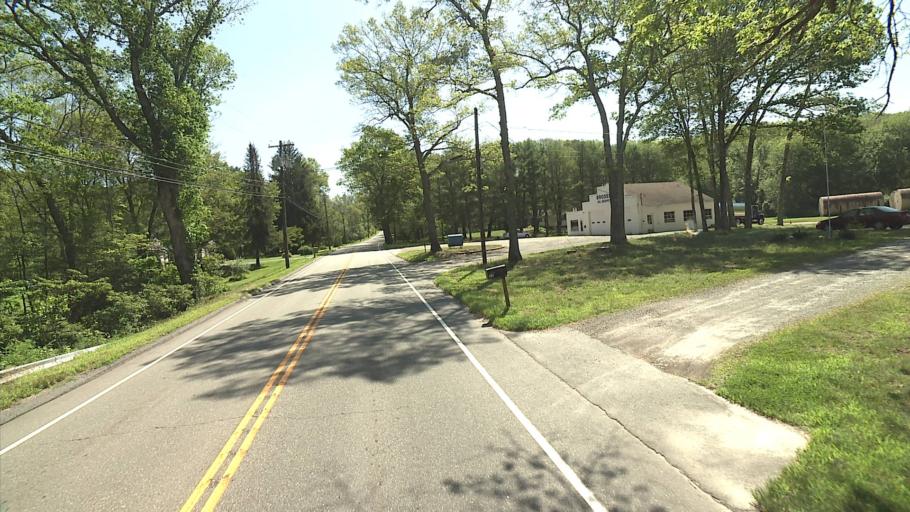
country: US
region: Connecticut
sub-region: Windham County
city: Moosup
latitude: 41.7192
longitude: -71.8546
